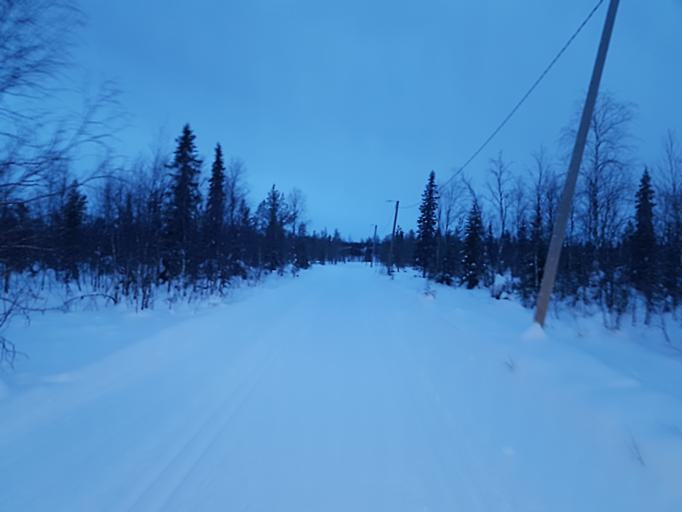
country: FI
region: Lapland
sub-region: Tunturi-Lappi
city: Kolari
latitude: 67.6144
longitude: 24.1656
